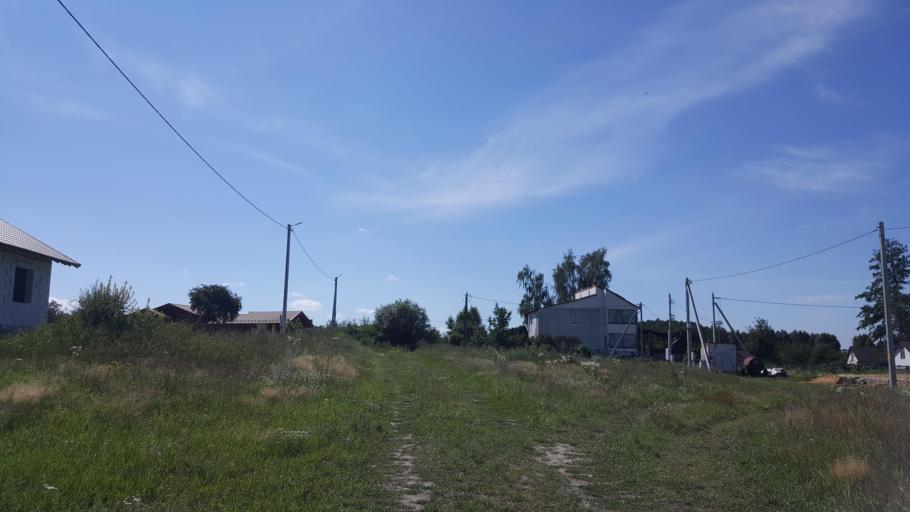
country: BY
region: Brest
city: Charnawchytsy
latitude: 52.2667
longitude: 23.7600
